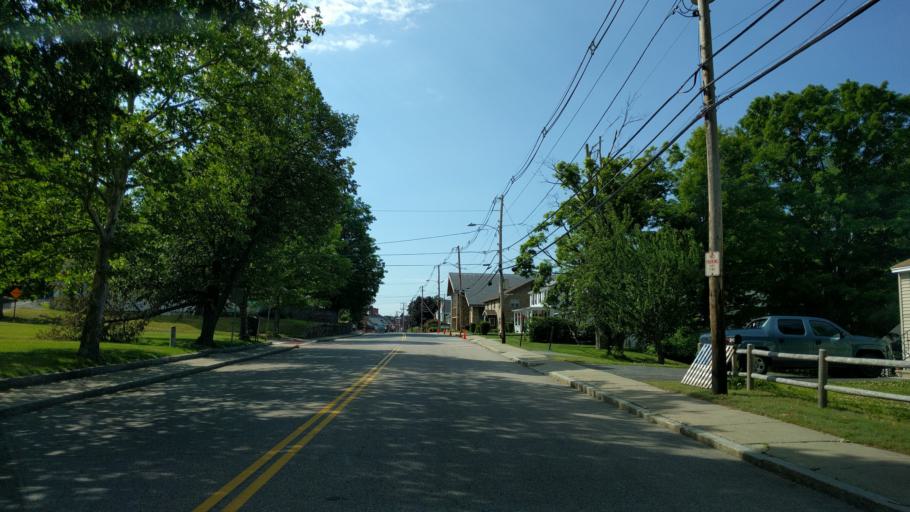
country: US
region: Massachusetts
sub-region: Worcester County
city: Millbury
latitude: 42.1962
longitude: -71.7632
